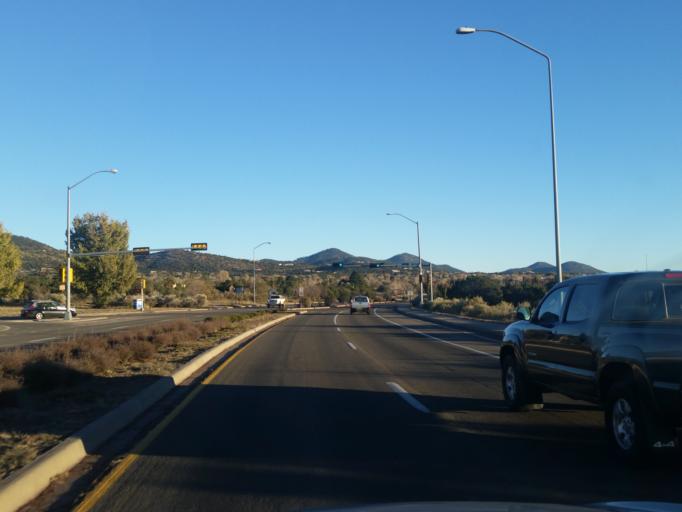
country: US
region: New Mexico
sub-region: Santa Fe County
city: Santa Fe
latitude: 35.6550
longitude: -105.9396
